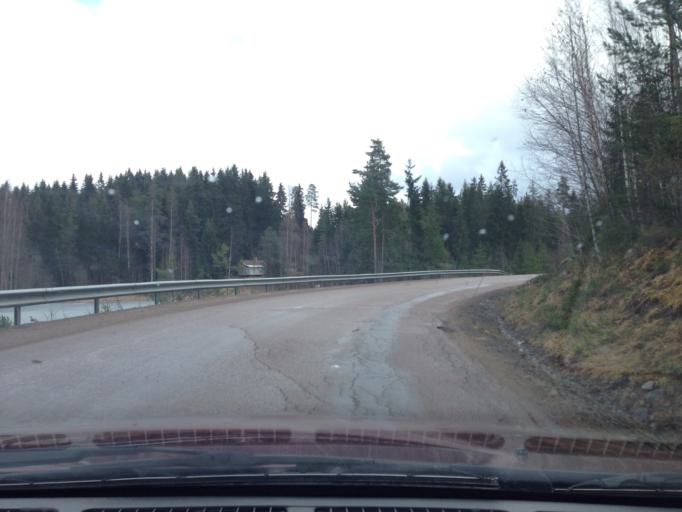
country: SE
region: Dalarna
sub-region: Ludvika Kommun
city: Ludvika
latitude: 60.1779
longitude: 15.2992
